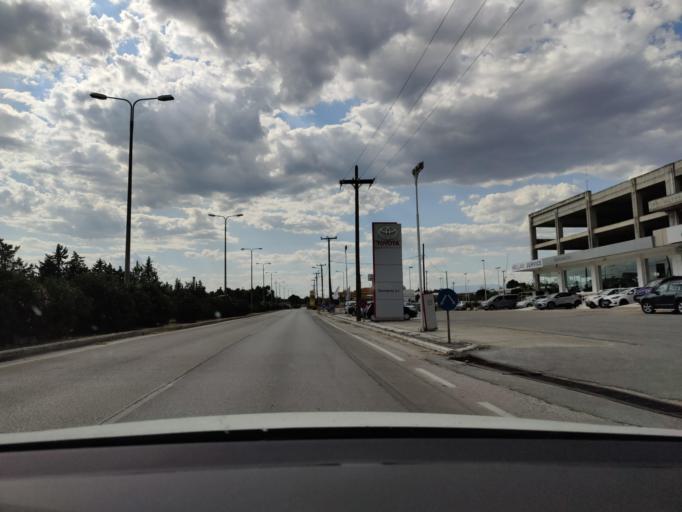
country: GR
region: Central Macedonia
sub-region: Nomos Serron
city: Lefkonas
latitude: 41.0915
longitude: 23.5136
